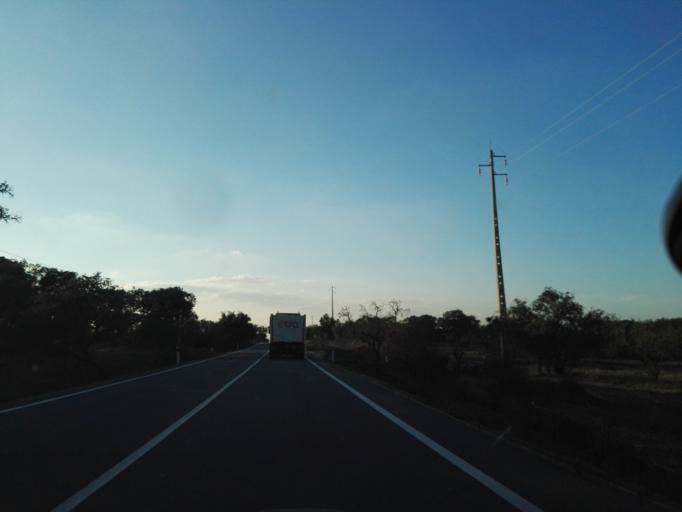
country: PT
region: Evora
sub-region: Arraiolos
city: Arraiolos
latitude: 38.8633
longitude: -7.9358
